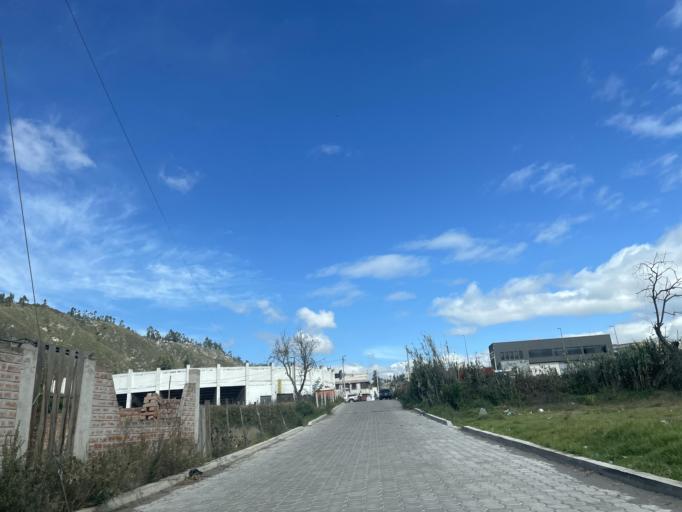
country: EC
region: Chimborazo
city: Guano
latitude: -1.6094
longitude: -78.6342
